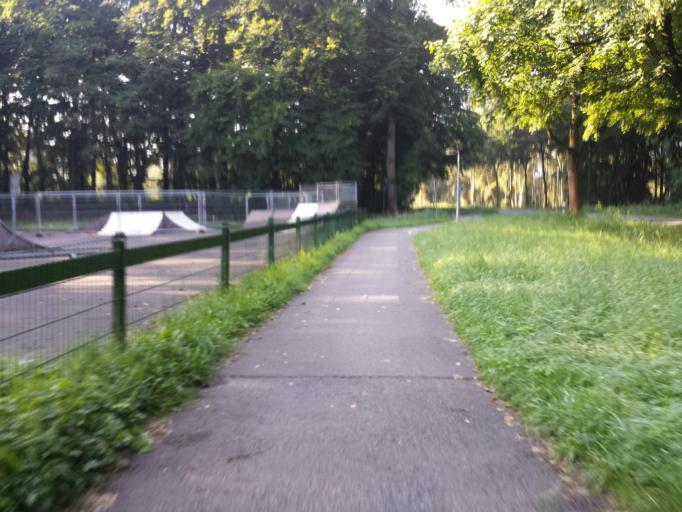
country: DE
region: North Rhine-Westphalia
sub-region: Regierungsbezirk Detmold
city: Harsewinkel
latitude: 51.9460
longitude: 8.2849
